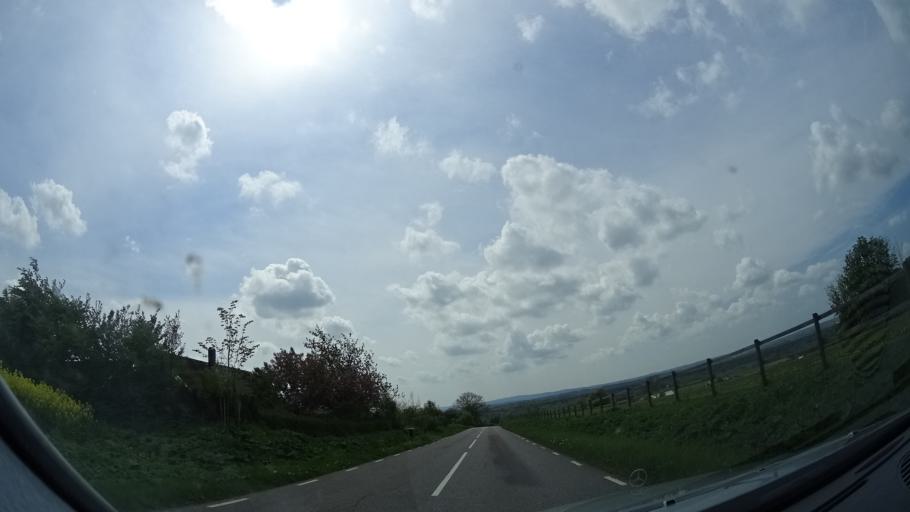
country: SE
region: Skane
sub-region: Hoors Kommun
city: Loberod
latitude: 55.7330
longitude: 13.4952
